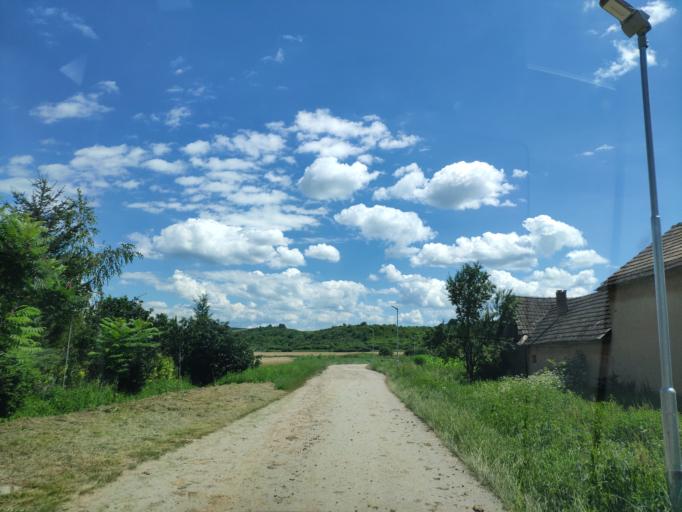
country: HU
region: Borsod-Abauj-Zemplen
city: Arlo
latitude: 48.2796
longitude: 20.1912
